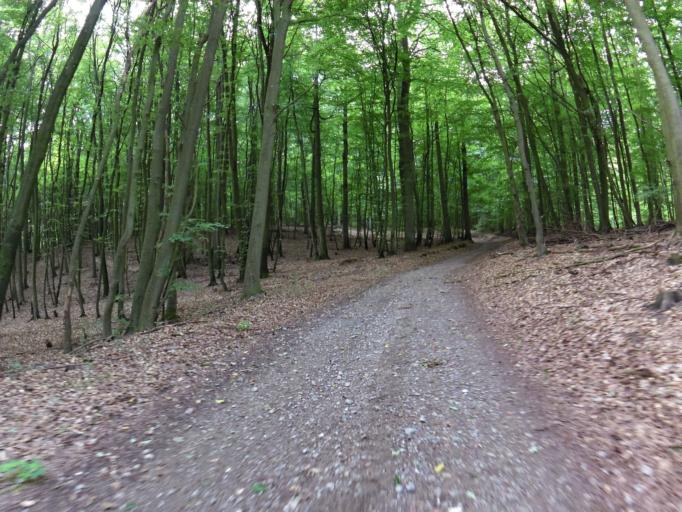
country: DE
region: Mecklenburg-Vorpommern
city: Seebad Bansin
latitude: 53.9548
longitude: 14.1065
